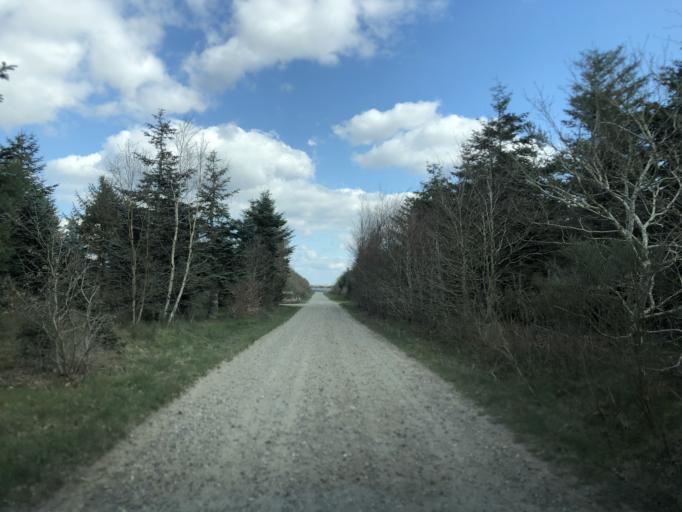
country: DK
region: Central Jutland
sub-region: Holstebro Kommune
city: Ulfborg
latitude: 56.3875
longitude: 8.2121
